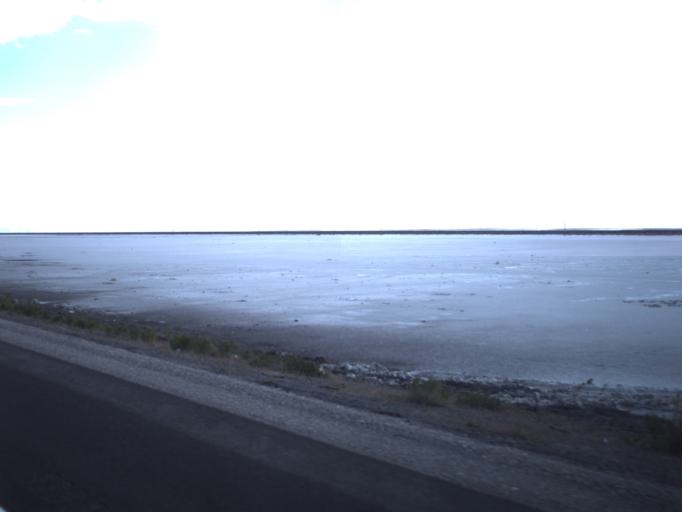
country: US
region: Utah
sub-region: Tooele County
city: Wendover
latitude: 40.7321
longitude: -113.5531
